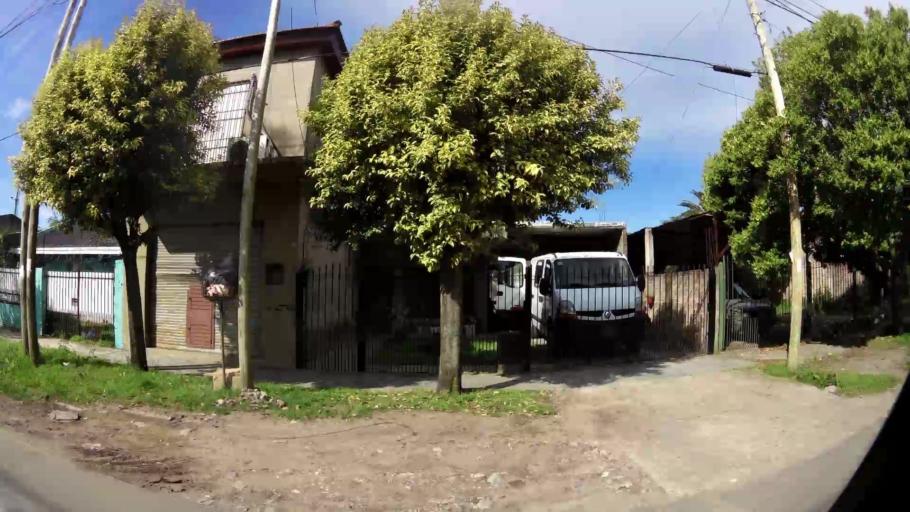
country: AR
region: Buenos Aires
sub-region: Partido de Almirante Brown
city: Adrogue
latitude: -34.8157
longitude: -58.3542
